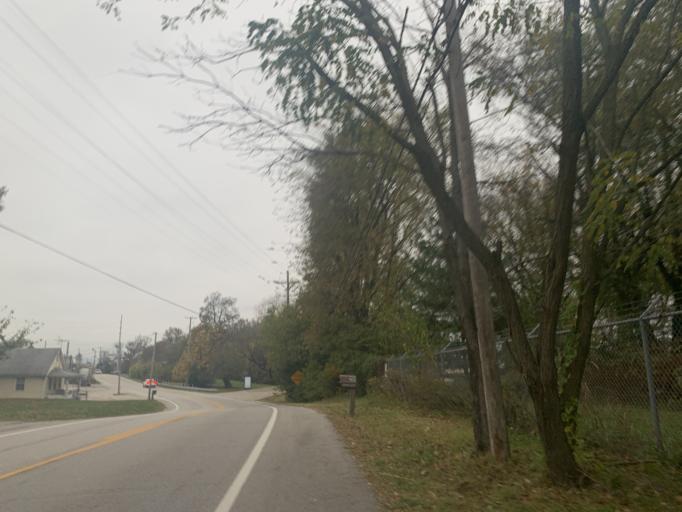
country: US
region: Kentucky
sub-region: Jefferson County
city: Shively
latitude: 38.2136
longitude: -85.8372
